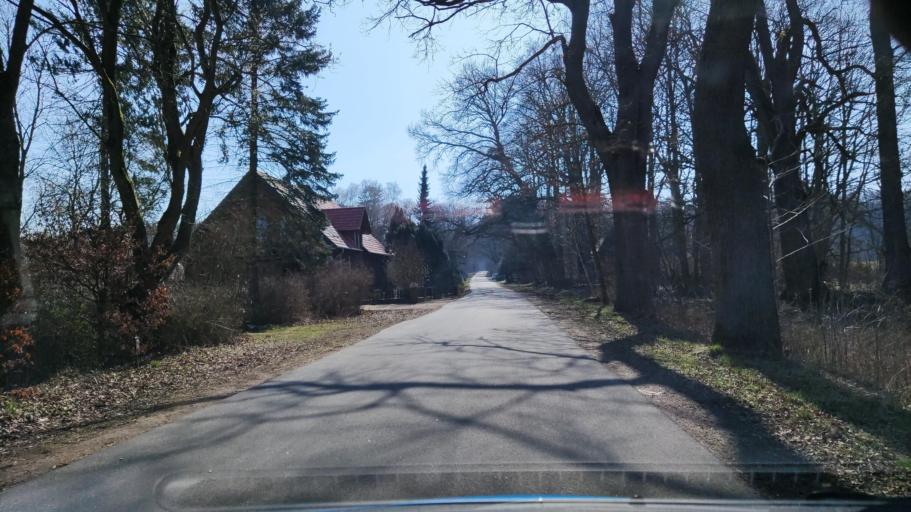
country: DE
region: Lower Saxony
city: Zernien
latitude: 52.9834
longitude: 10.8733
